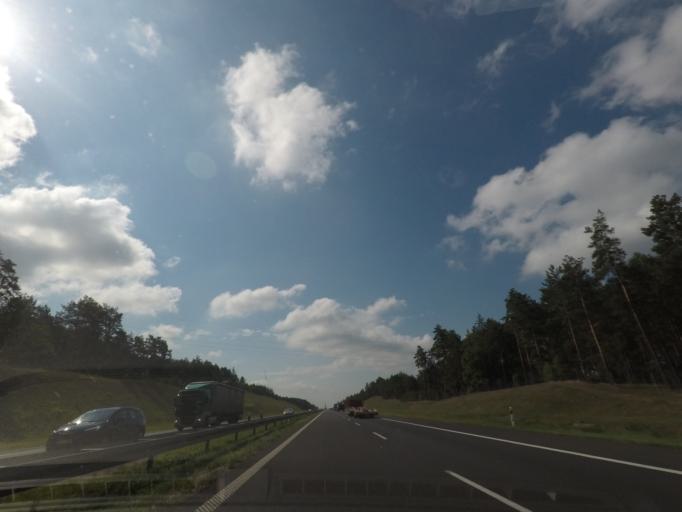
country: PL
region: Kujawsko-Pomorskie
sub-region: Powiat swiecki
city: Warlubie
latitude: 53.4872
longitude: 18.6161
